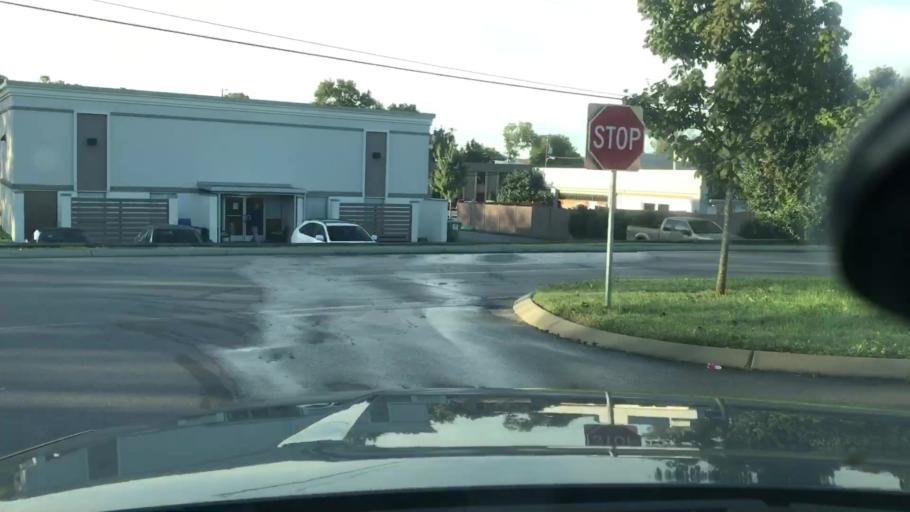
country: US
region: Tennessee
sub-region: Williamson County
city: Brentwood
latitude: 36.0282
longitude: -86.7850
